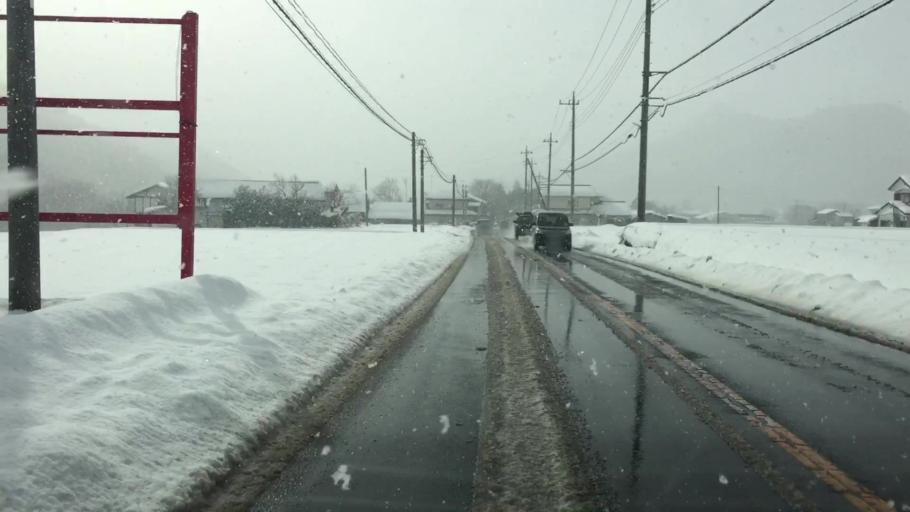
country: JP
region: Gunma
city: Numata
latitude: 36.7029
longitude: 139.0655
